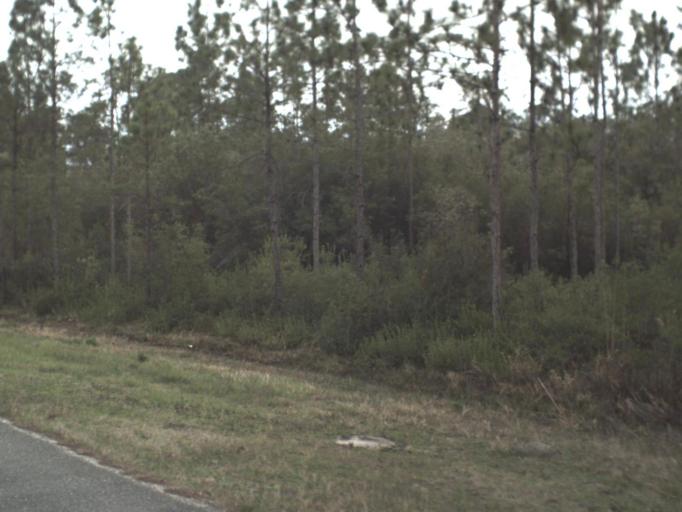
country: US
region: Florida
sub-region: Gadsden County
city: Midway
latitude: 30.3725
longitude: -84.5516
